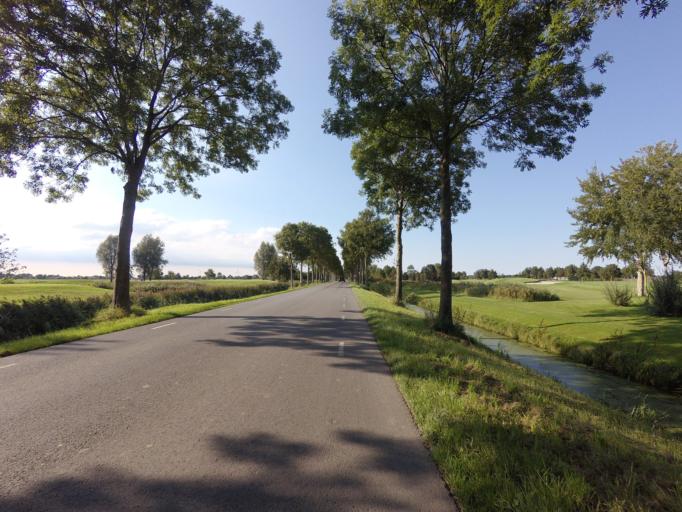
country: NL
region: North Holland
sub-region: Gemeente Hoorn
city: Hoorn
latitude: 52.6695
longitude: 5.1423
